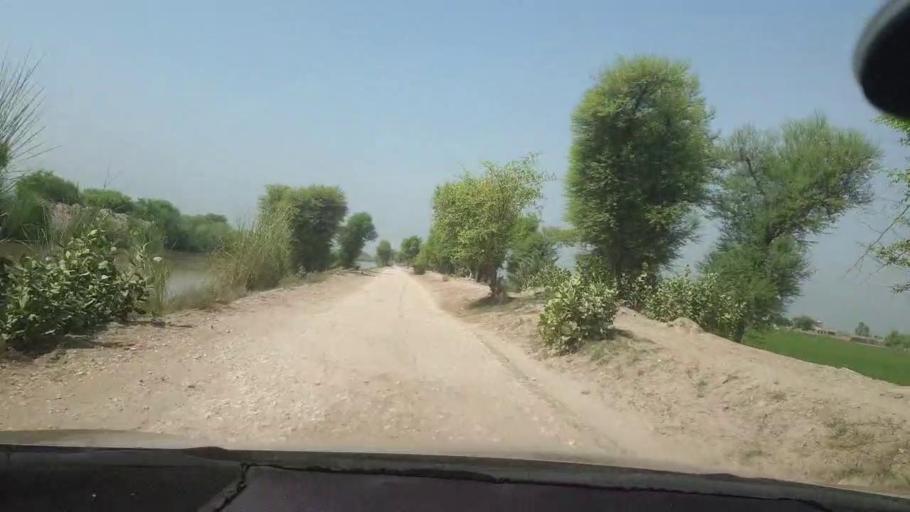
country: PK
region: Sindh
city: Shahdadkot
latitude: 27.7258
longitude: 67.9590
